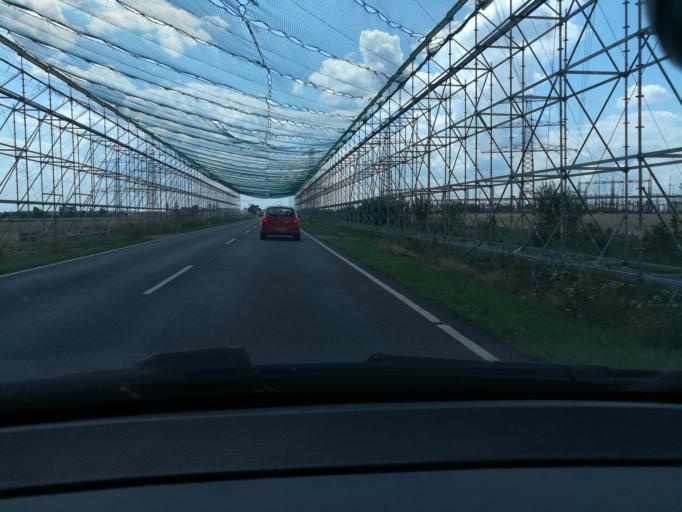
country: DE
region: Saxony-Anhalt
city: Wolmirstedt
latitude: 52.2698
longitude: 11.6458
